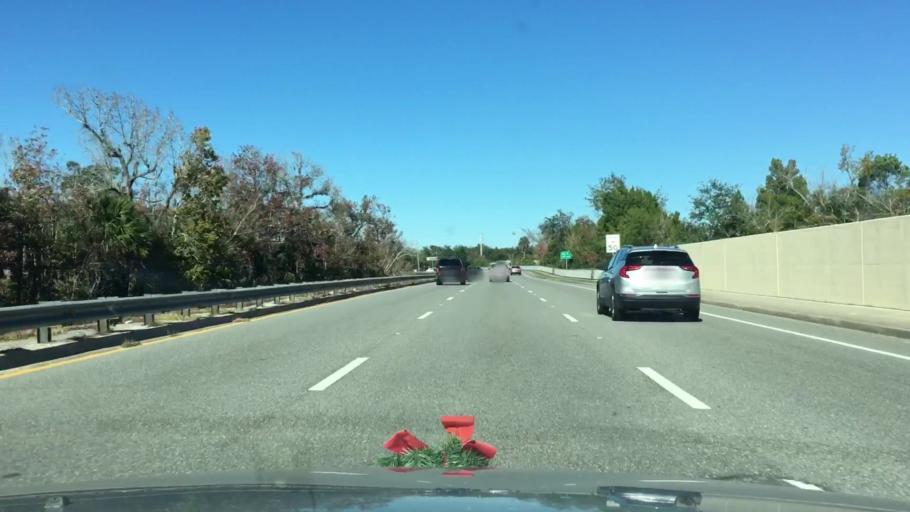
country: US
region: Florida
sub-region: Volusia County
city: South Daytona
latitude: 29.1636
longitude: -81.0231
